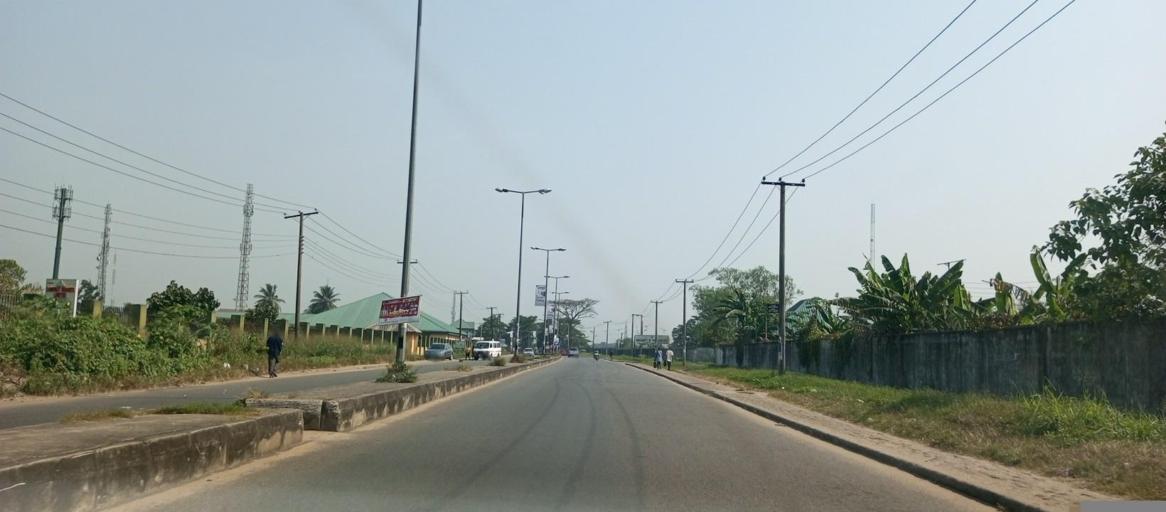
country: NG
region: Rivers
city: Emuoha
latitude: 4.8933
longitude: 6.9068
